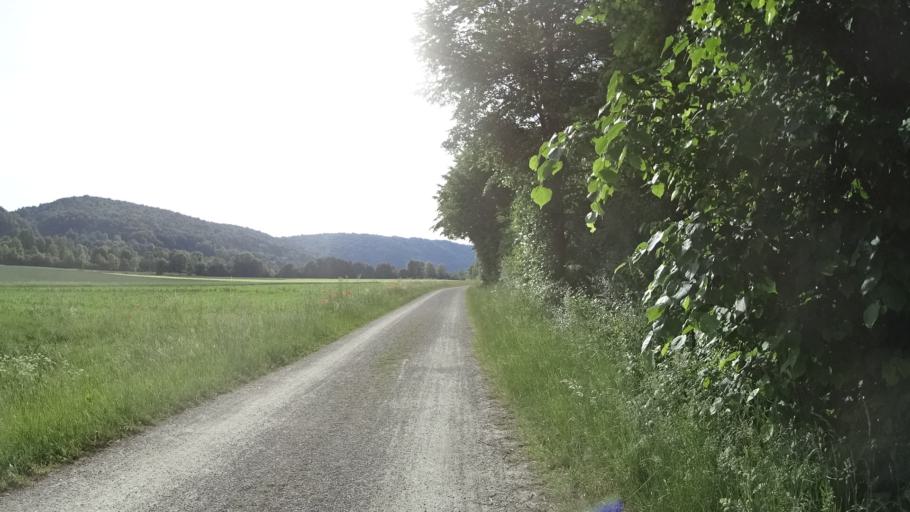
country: DE
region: Bavaria
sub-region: Lower Bavaria
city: Riedenburg
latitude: 48.9559
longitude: 11.7086
